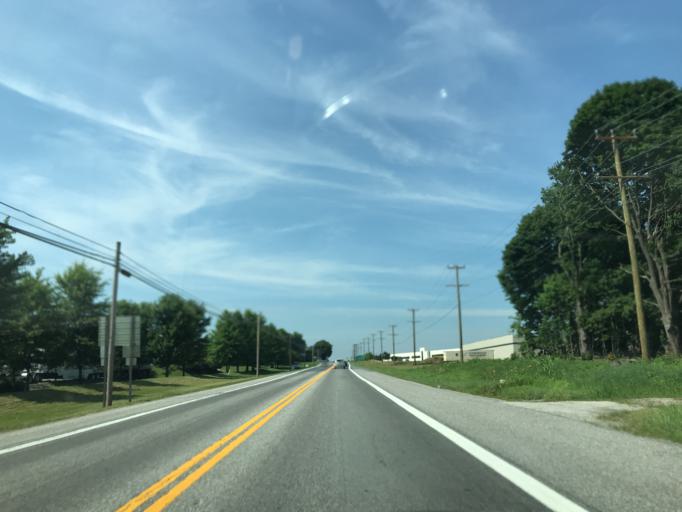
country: US
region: Maryland
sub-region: Carroll County
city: Westminster
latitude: 39.6091
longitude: -76.9980
